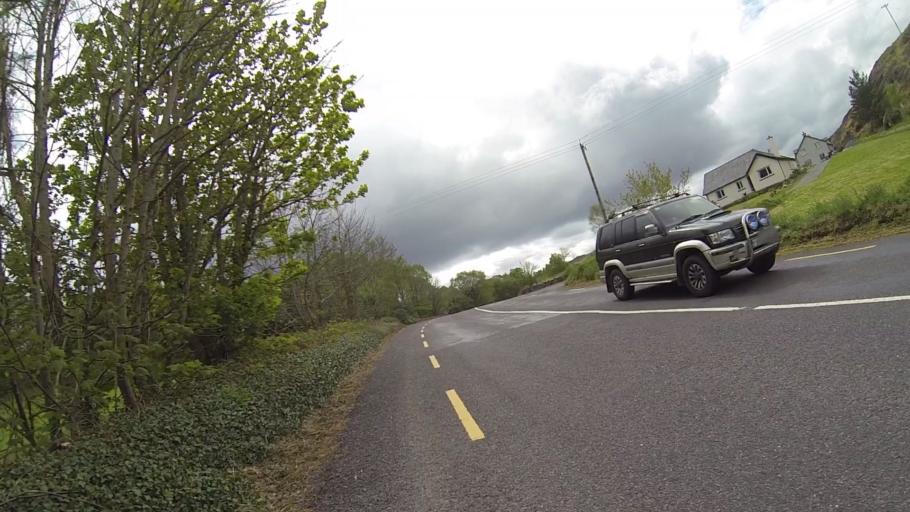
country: IE
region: Munster
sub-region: County Cork
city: Bantry
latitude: 51.7416
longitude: -9.5509
